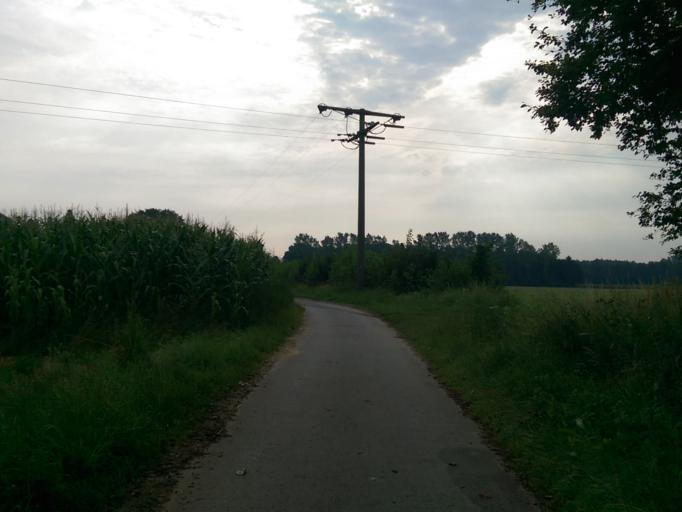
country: DE
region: North Rhine-Westphalia
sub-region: Regierungsbezirk Detmold
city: Guetersloh
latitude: 51.9489
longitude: 8.3172
